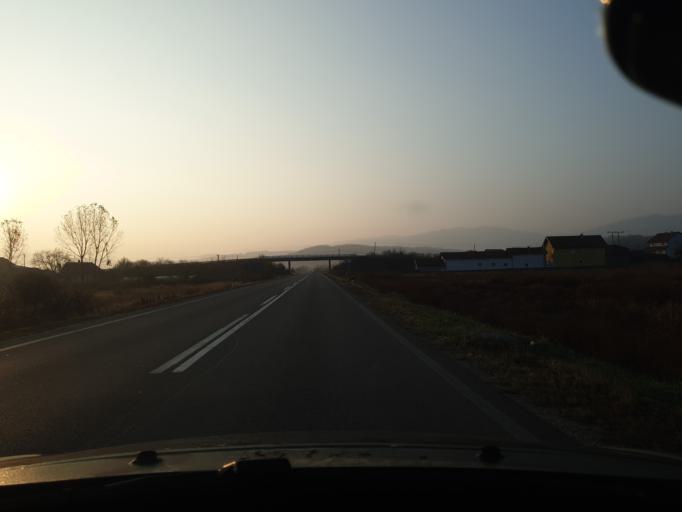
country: RS
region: Central Serbia
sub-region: Jablanicki Okrug
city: Leskovac
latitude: 42.9296
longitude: 22.0152
